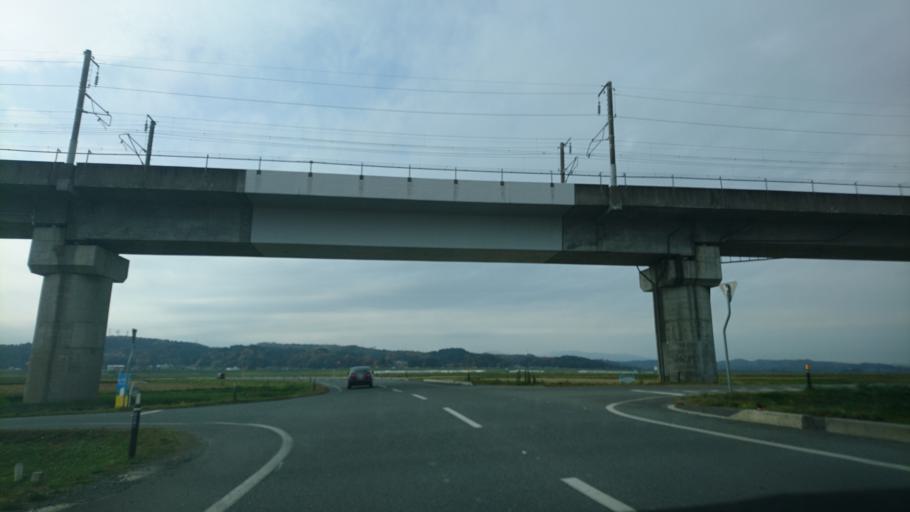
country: JP
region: Iwate
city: Ichinoseki
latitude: 38.9475
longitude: 141.1482
